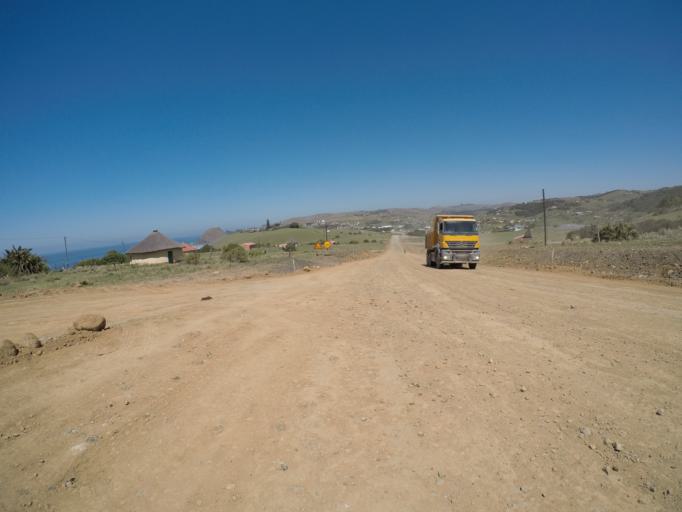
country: ZA
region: Eastern Cape
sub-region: OR Tambo District Municipality
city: Libode
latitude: -32.0272
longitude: 29.1161
